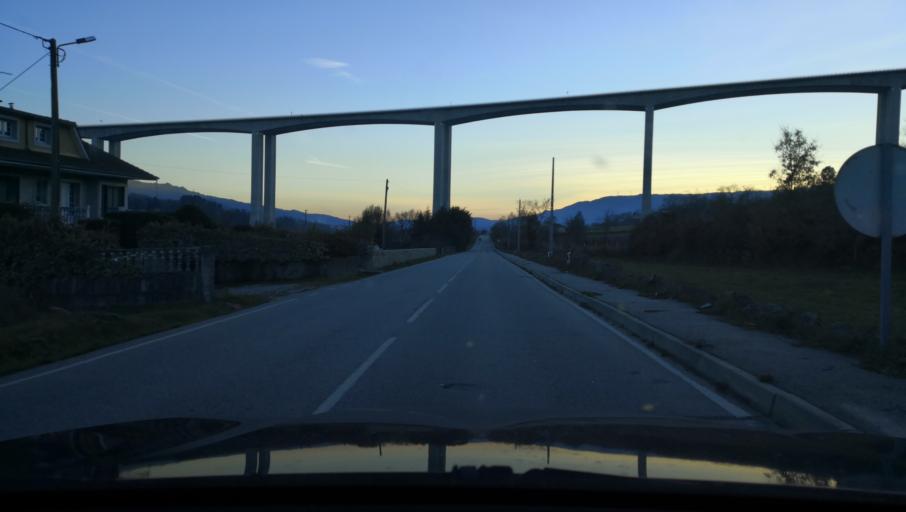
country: PT
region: Vila Real
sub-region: Vila Pouca de Aguiar
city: Vila Pouca de Aguiar
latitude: 41.4859
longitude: -7.6514
